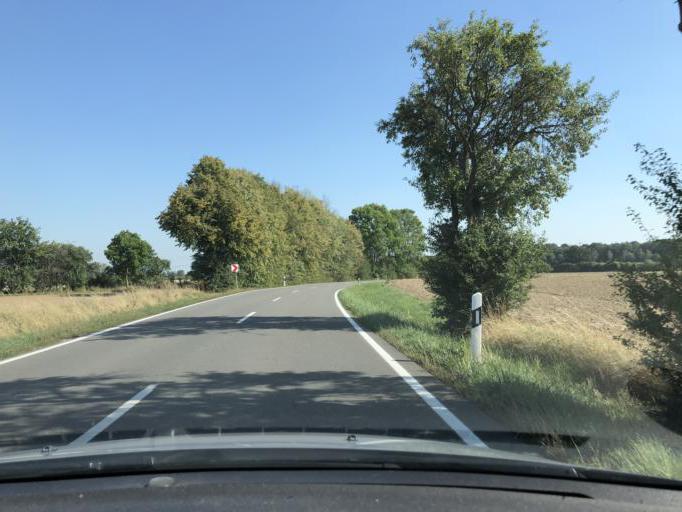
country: DE
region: Thuringia
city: Rastenberg
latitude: 51.1881
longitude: 11.4932
